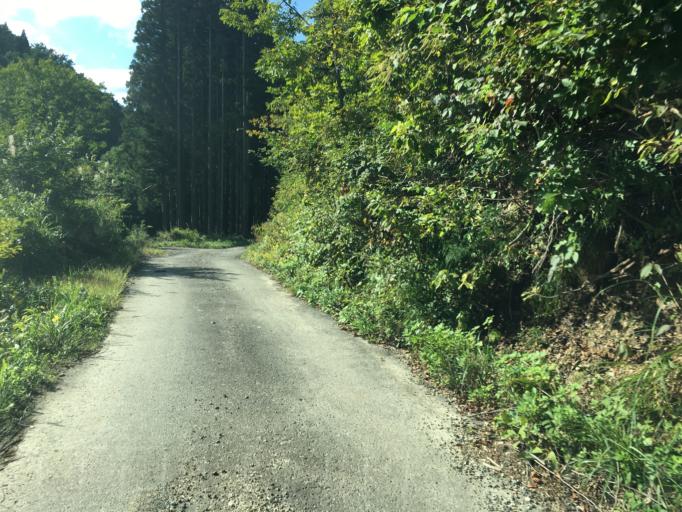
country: JP
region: Yamagata
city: Yonezawa
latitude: 37.8248
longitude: 140.2232
